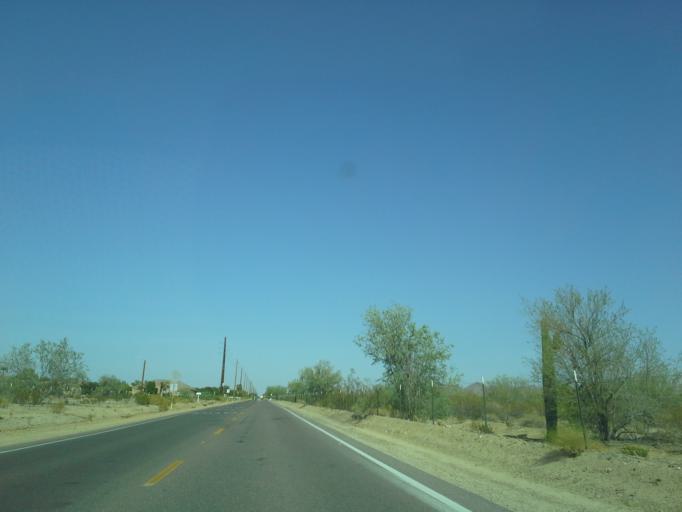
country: US
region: Arizona
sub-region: Maricopa County
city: Queen Creek
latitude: 33.2046
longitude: -111.7146
